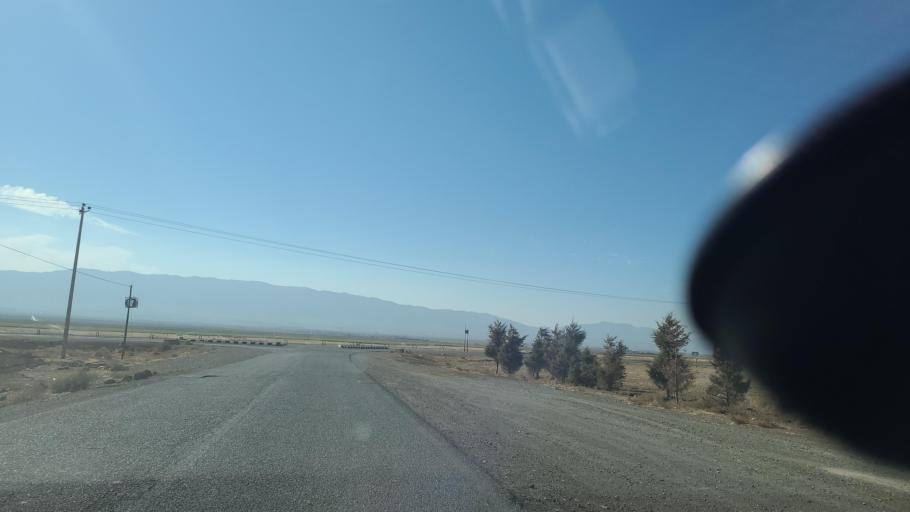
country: IR
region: Razavi Khorasan
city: Dowlatabad
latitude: 35.6009
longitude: 59.4605
